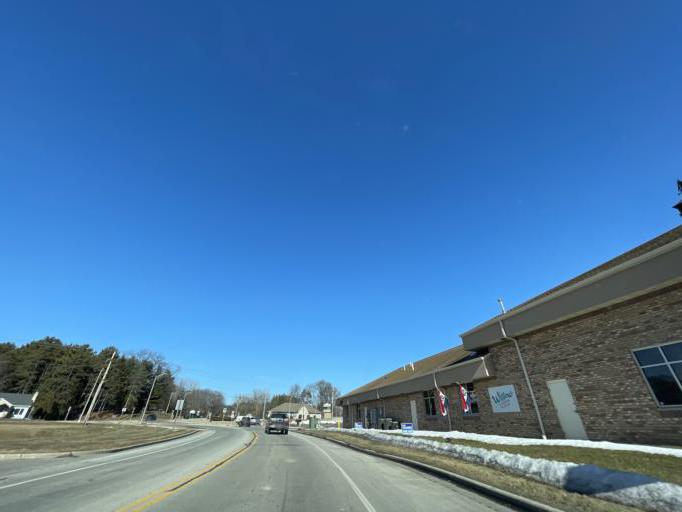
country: US
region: Wisconsin
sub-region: Brown County
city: Suamico
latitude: 44.6337
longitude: -88.0524
